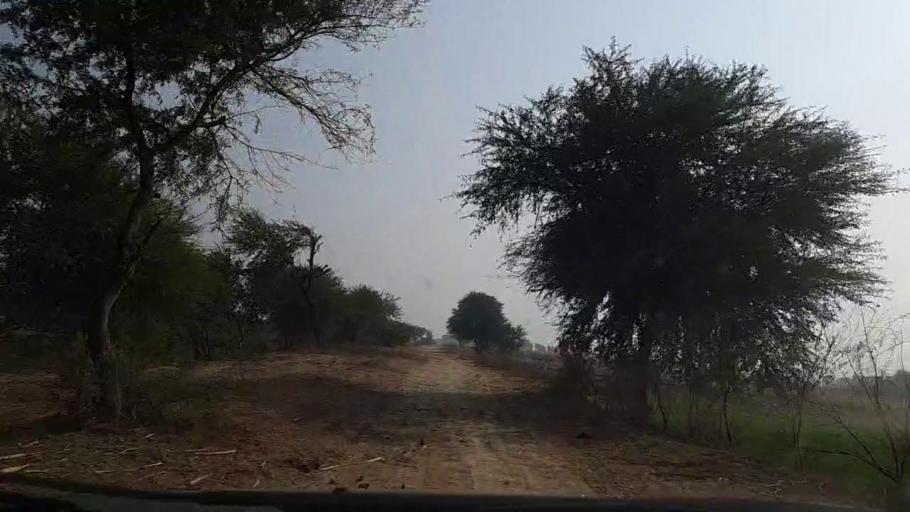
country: PK
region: Sindh
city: Sanghar
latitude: 26.0442
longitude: 68.9909
